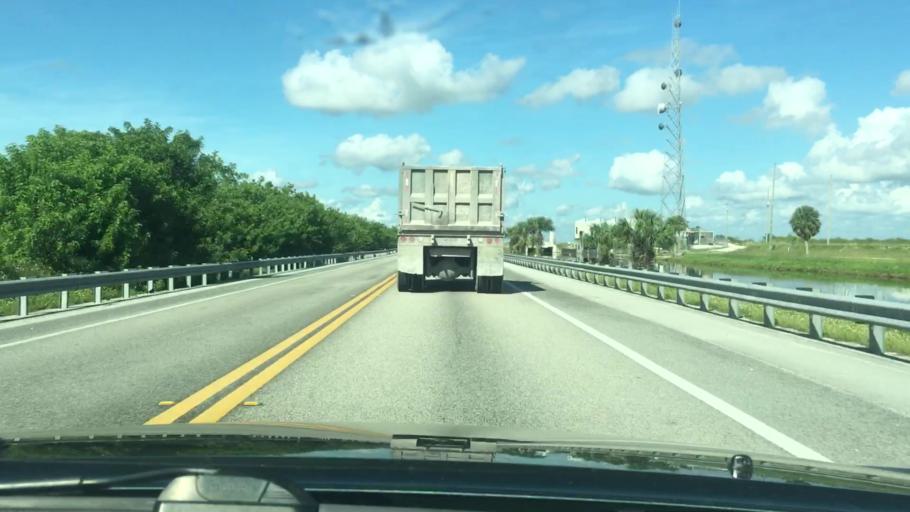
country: US
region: Florida
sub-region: Miami-Dade County
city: Kendall West
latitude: 25.7607
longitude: -80.4998
